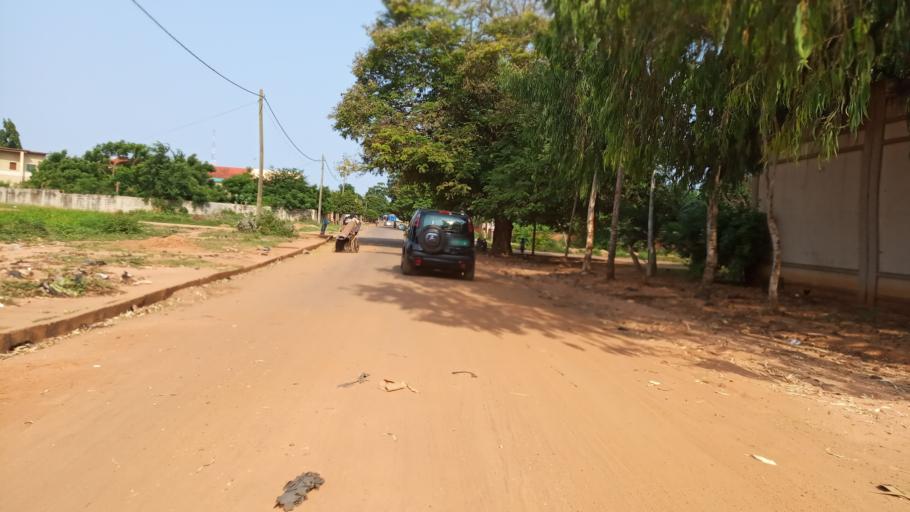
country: TG
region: Maritime
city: Lome
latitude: 6.2067
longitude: 1.2039
